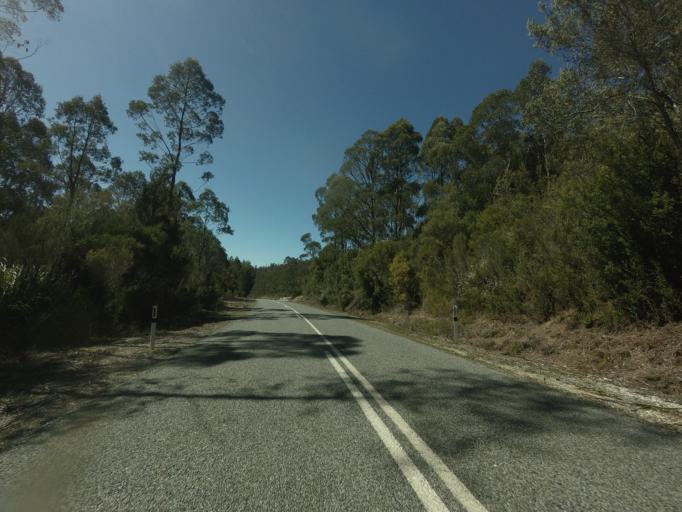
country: AU
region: Tasmania
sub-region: Derwent Valley
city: New Norfolk
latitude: -42.7556
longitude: 146.4097
